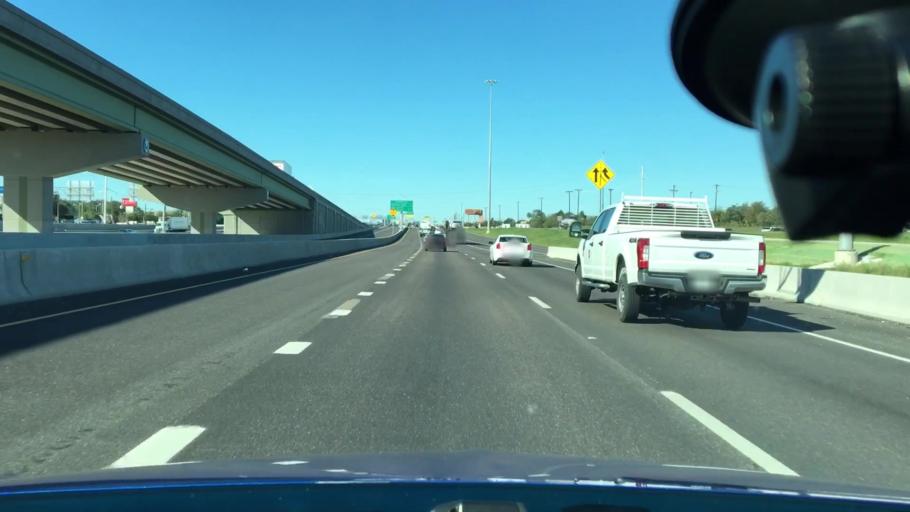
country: US
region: Texas
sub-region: Dallas County
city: Irving
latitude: 32.8373
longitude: -96.9196
